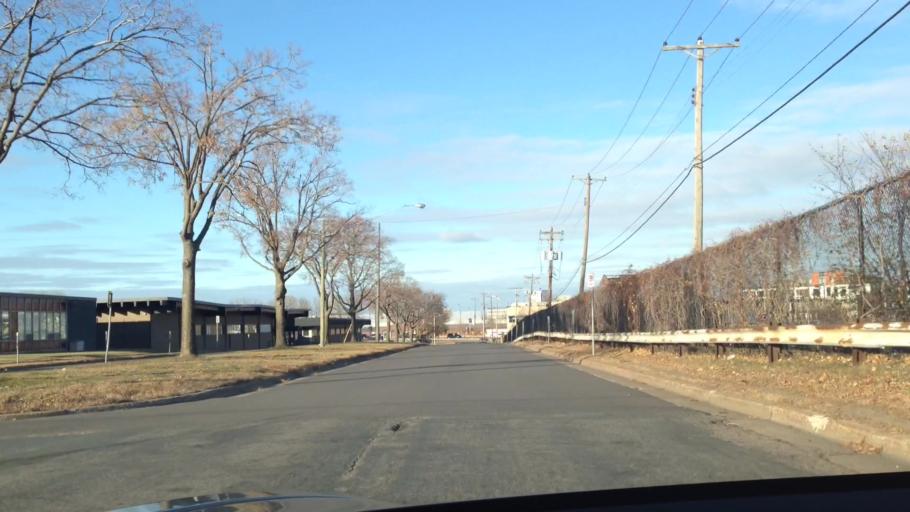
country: US
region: Minnesota
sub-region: Hennepin County
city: Minneapolis
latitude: 44.9812
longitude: -93.2830
